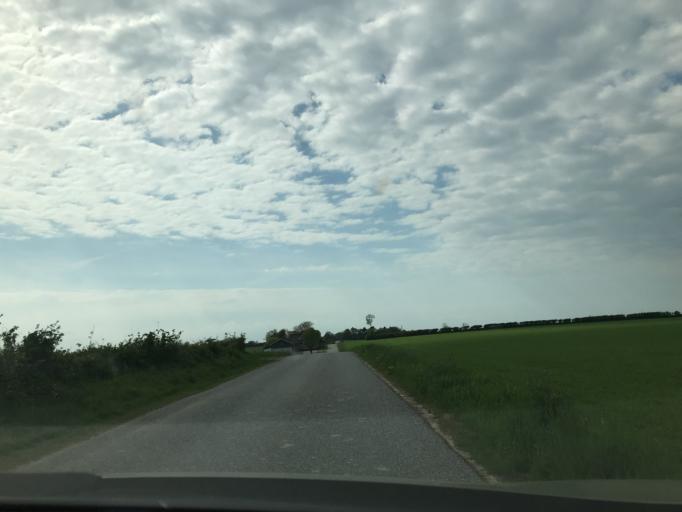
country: DK
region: South Denmark
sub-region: Middelfart Kommune
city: Ejby
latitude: 55.3611
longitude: 9.8616
